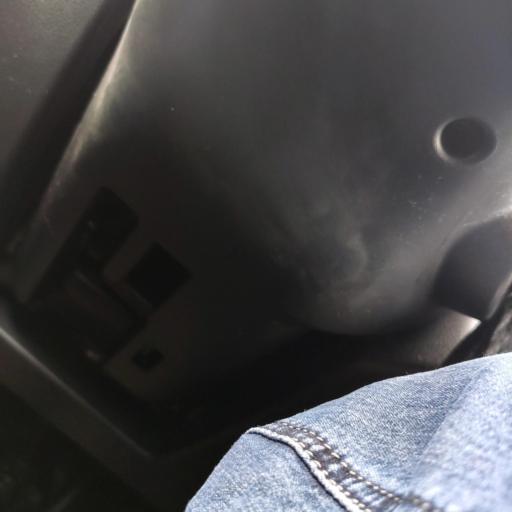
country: RU
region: Samara
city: Smyshlyayevka
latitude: 53.2116
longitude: 50.3275
